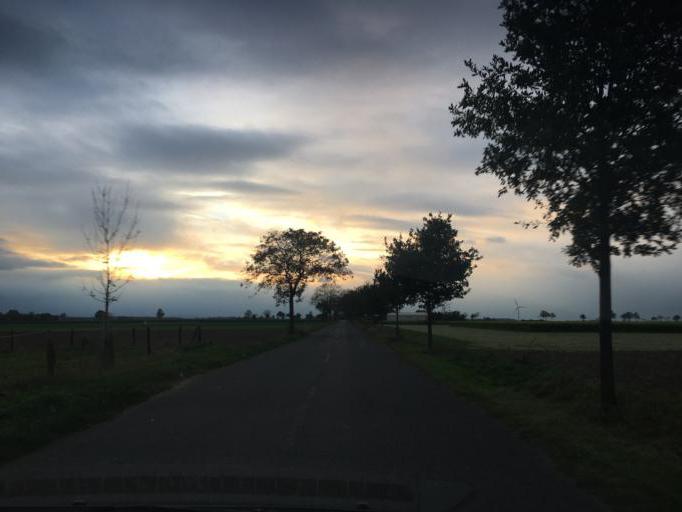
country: DE
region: North Rhine-Westphalia
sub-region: Regierungsbezirk Koln
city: Norvenich
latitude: 50.7664
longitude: 6.7149
